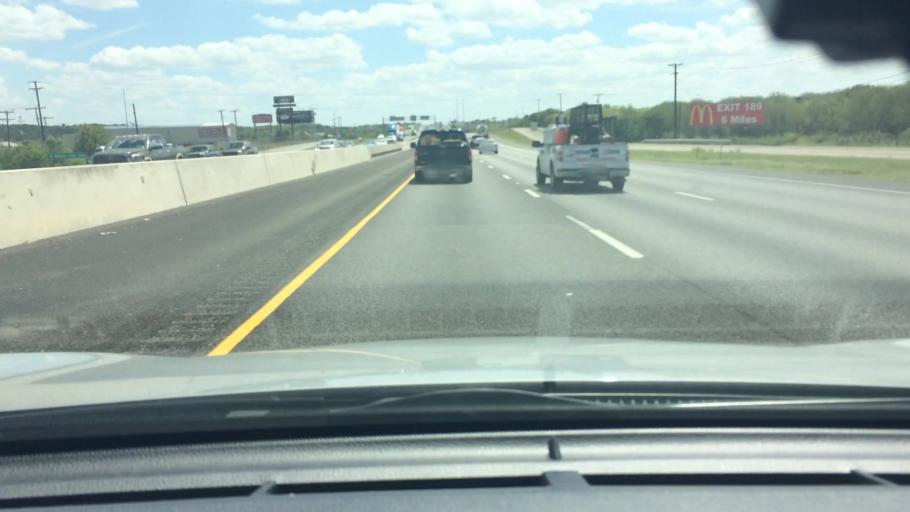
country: US
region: Texas
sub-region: Guadalupe County
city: Lake Dunlap
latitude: 29.7733
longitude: -98.0395
